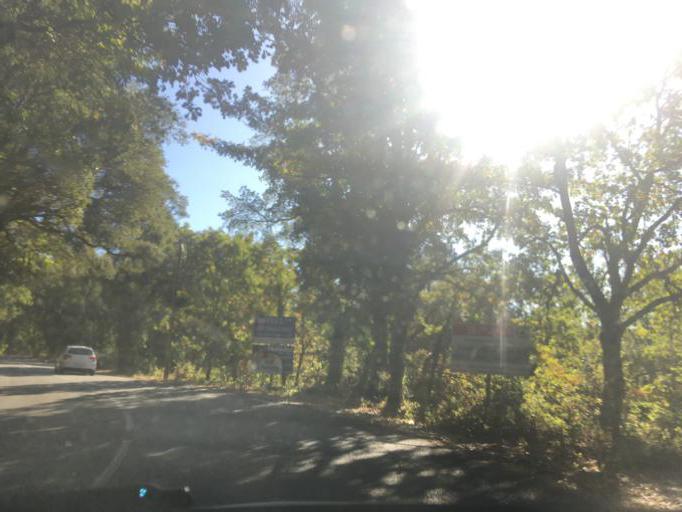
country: FR
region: Provence-Alpes-Cote d'Azur
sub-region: Departement du Var
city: La Garde-Freinet
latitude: 43.3266
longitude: 6.4721
